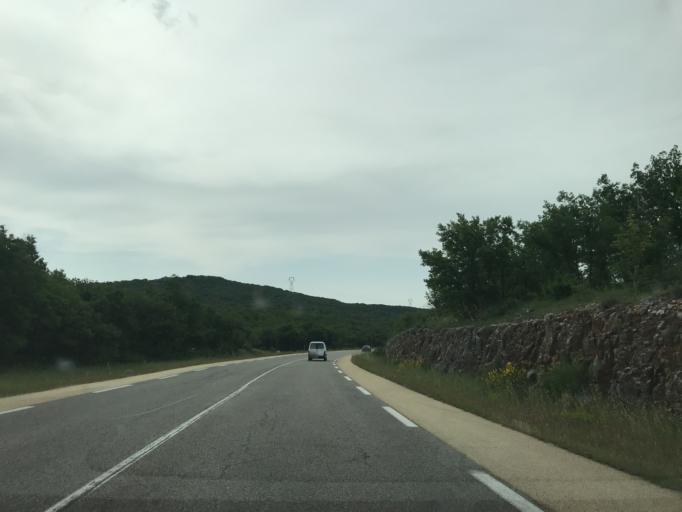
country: FR
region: Provence-Alpes-Cote d'Azur
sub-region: Departement du Var
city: Pourrieres
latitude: 43.5416
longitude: 5.8102
